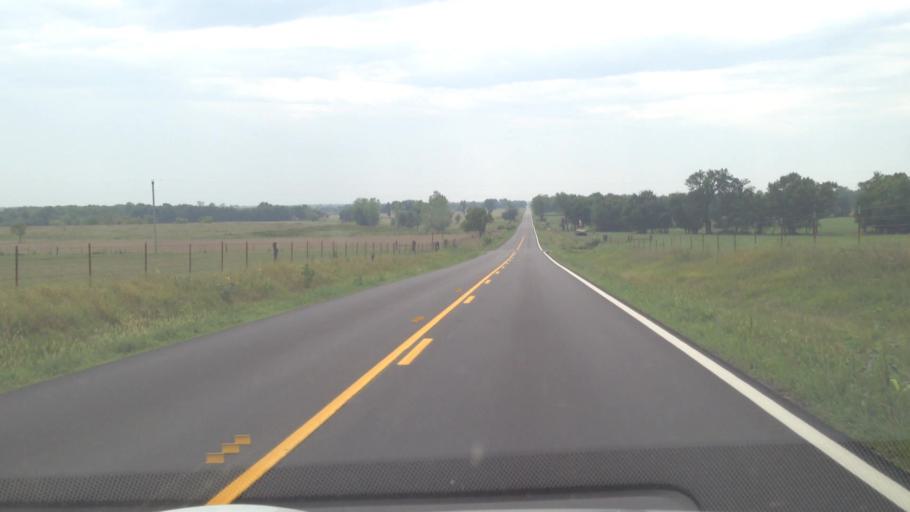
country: US
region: Kansas
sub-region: Crawford County
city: Girard
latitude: 37.5448
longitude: -94.9605
